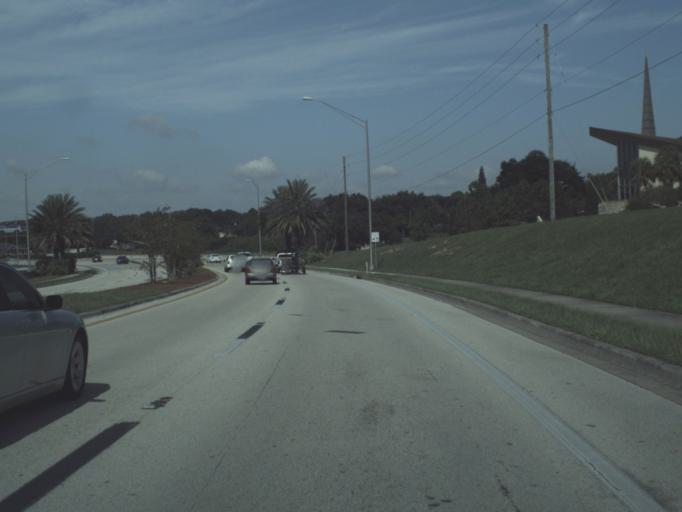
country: US
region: Florida
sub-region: Polk County
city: Cypress Gardens
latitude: 28.0037
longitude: -81.6969
